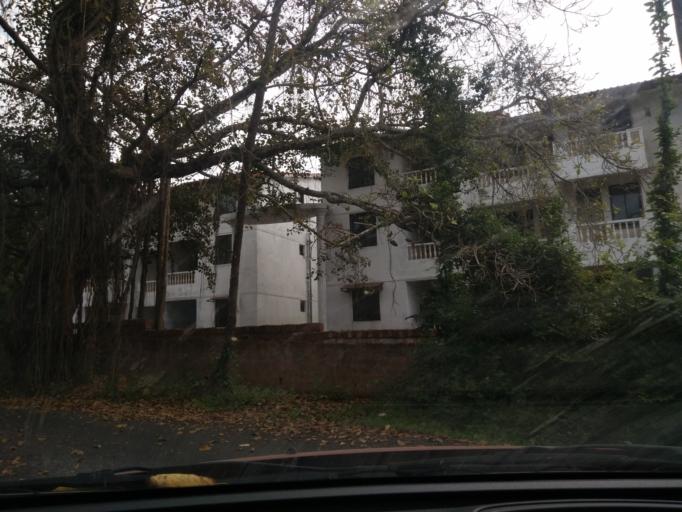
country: IN
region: Goa
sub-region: South Goa
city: Varca
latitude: 15.2268
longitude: 73.9545
